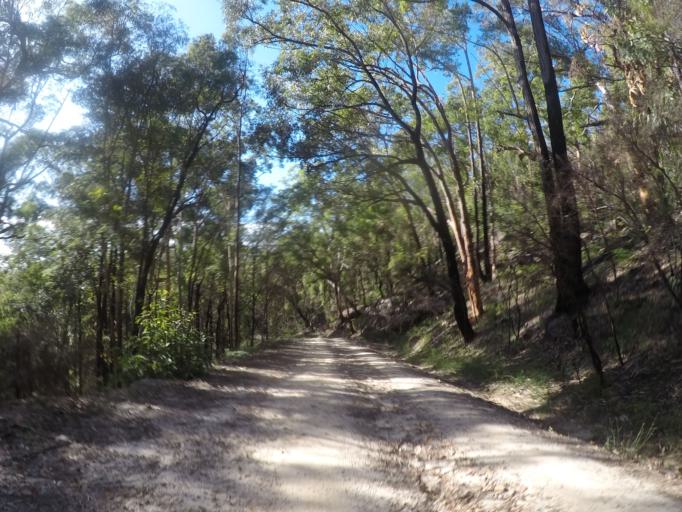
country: AU
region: New South Wales
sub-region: Gosford Shire
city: Point Clare
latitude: -33.3356
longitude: 151.0767
